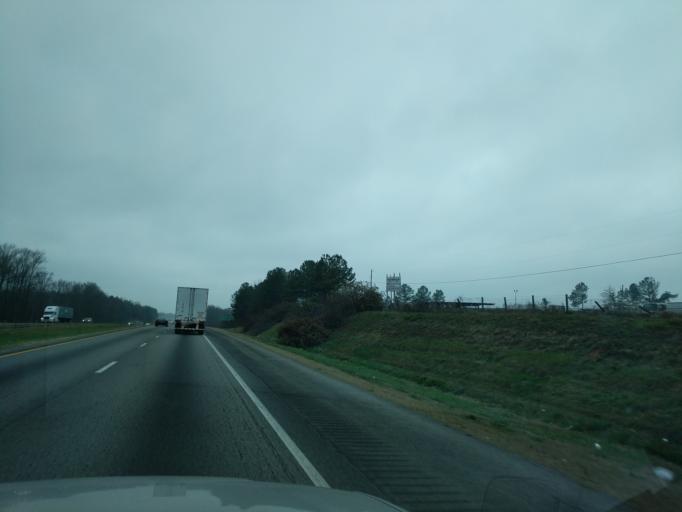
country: US
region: Georgia
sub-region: Jackson County
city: Jefferson
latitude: 34.1803
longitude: -83.6035
